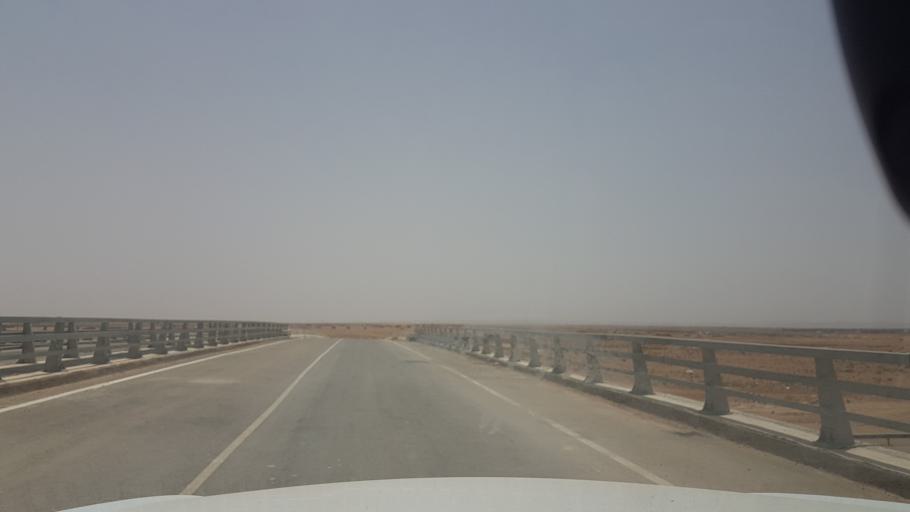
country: TN
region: Madanin
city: Medenine
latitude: 33.3000
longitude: 10.6093
